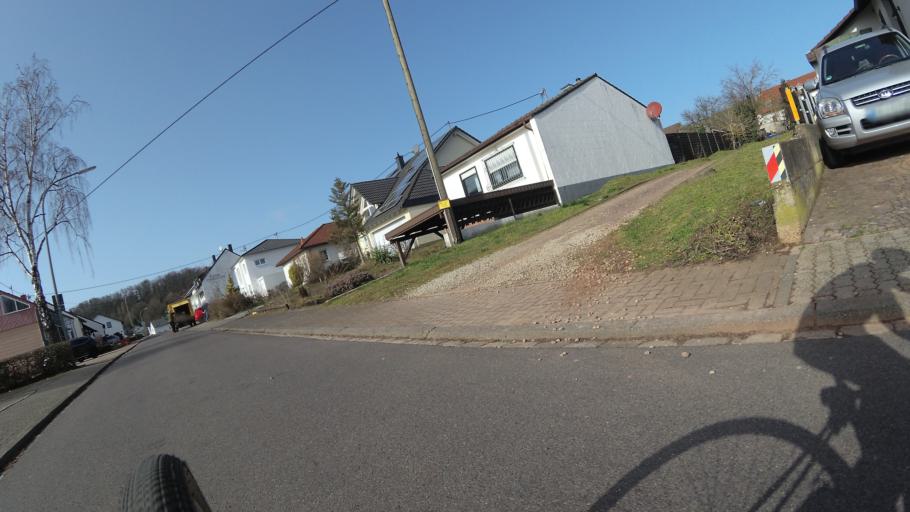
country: DE
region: Saarland
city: Uberherrn
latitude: 49.2749
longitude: 6.7036
